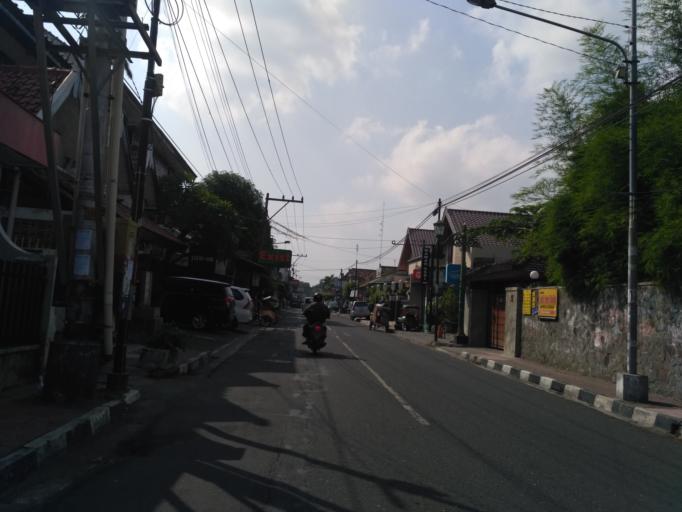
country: ID
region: Daerah Istimewa Yogyakarta
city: Yogyakarta
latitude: -7.8043
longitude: 110.3586
